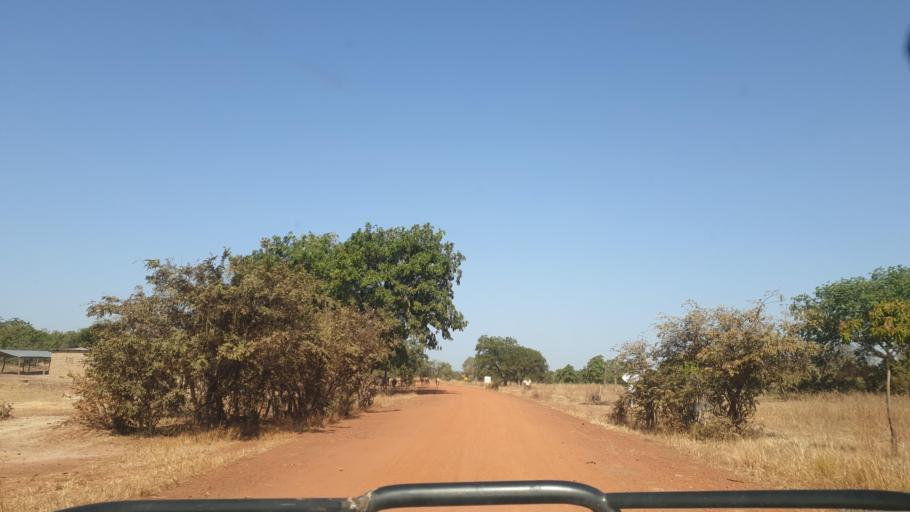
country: ML
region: Sikasso
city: Bougouni
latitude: 11.8154
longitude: -6.9368
